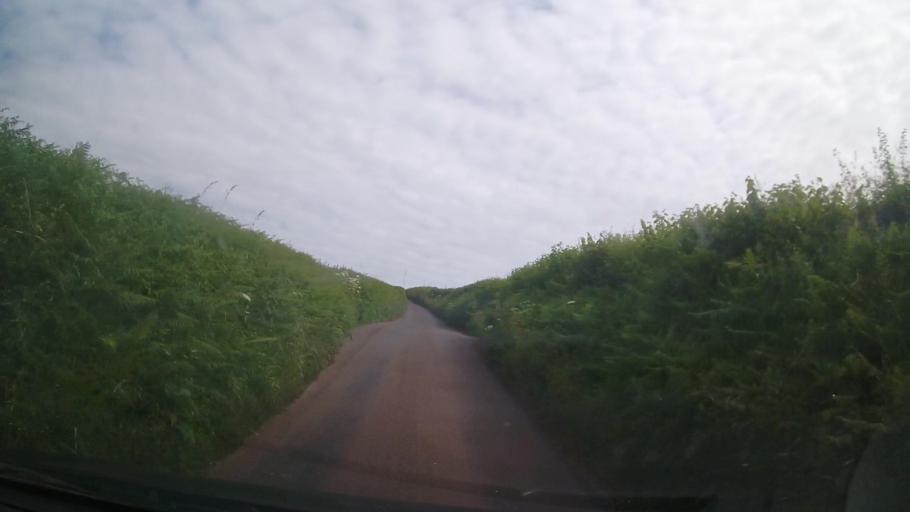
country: GB
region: England
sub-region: Devon
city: Salcombe
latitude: 50.2353
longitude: -3.6735
